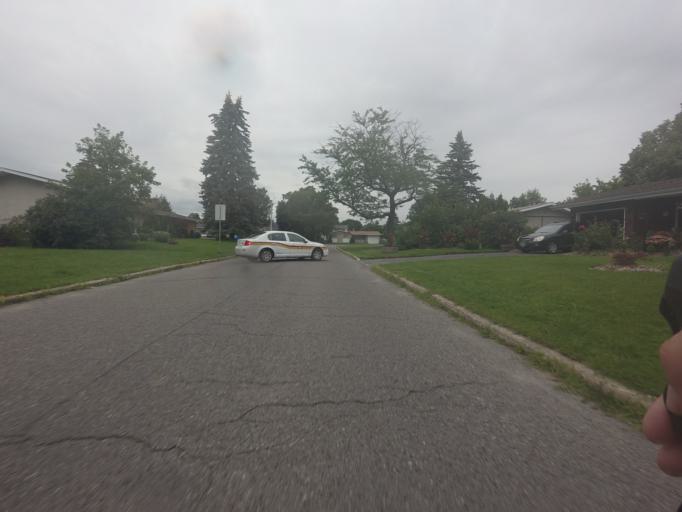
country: CA
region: Ontario
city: Ottawa
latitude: 45.3584
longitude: -75.7236
